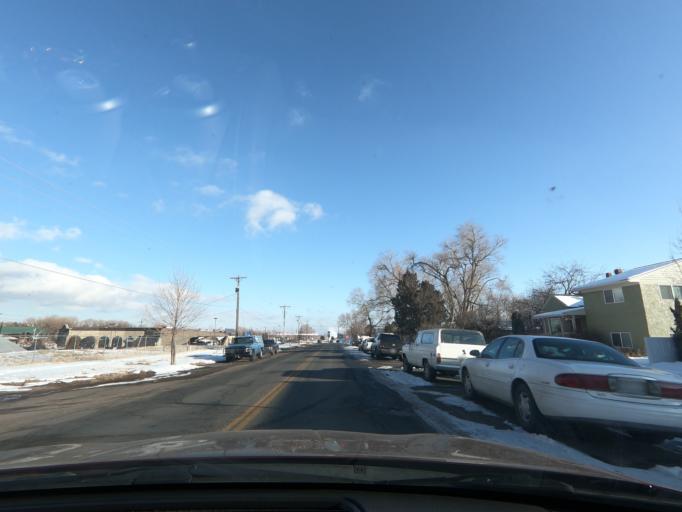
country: US
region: Colorado
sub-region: El Paso County
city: Colorado Springs
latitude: 38.8401
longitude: -104.8616
